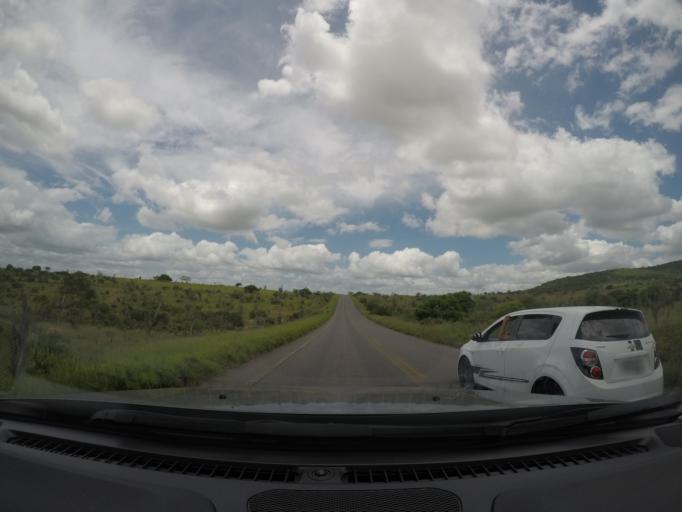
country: BR
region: Bahia
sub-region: Ipira
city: Ipira
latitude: -12.2640
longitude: -39.8313
